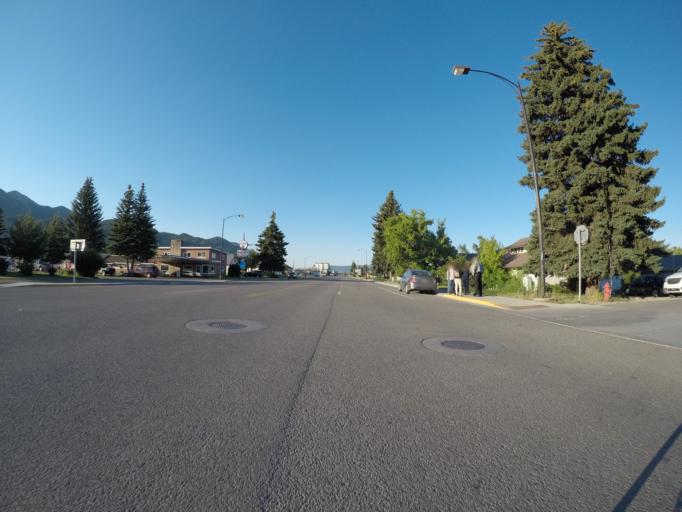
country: US
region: Wyoming
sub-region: Lincoln County
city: Afton
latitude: 42.7295
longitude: -110.9334
